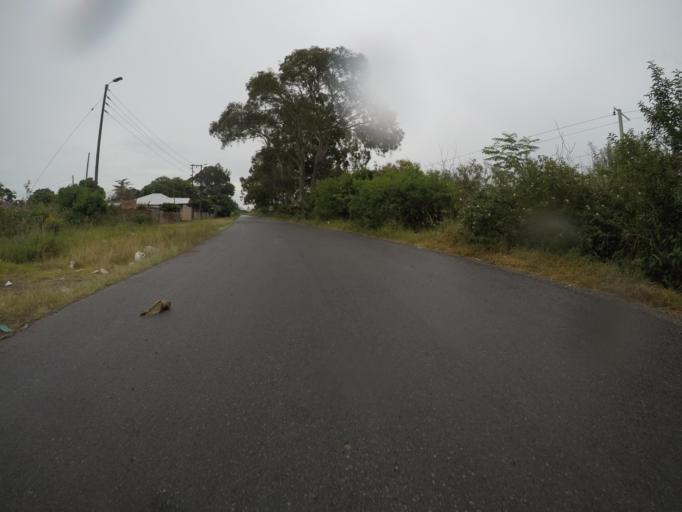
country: ZA
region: Eastern Cape
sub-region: Buffalo City Metropolitan Municipality
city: East London
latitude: -32.9673
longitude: 27.8169
